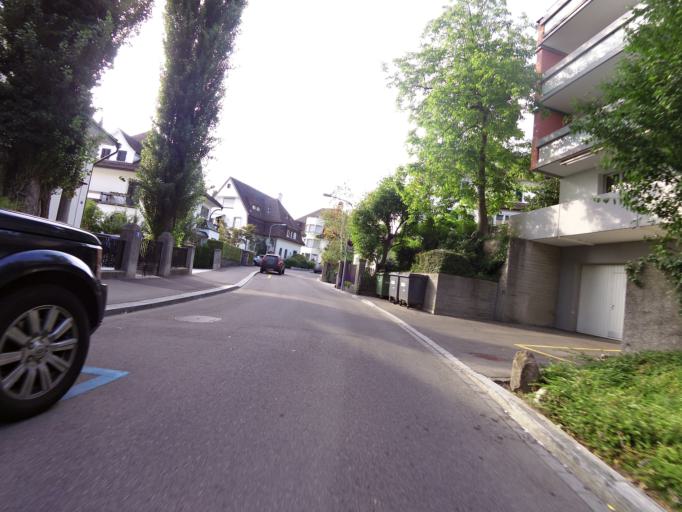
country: CH
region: Zurich
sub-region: Bezirk Zuerich
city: Zuerich (Kreis 6) / Oberstrass
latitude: 47.3865
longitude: 8.5502
